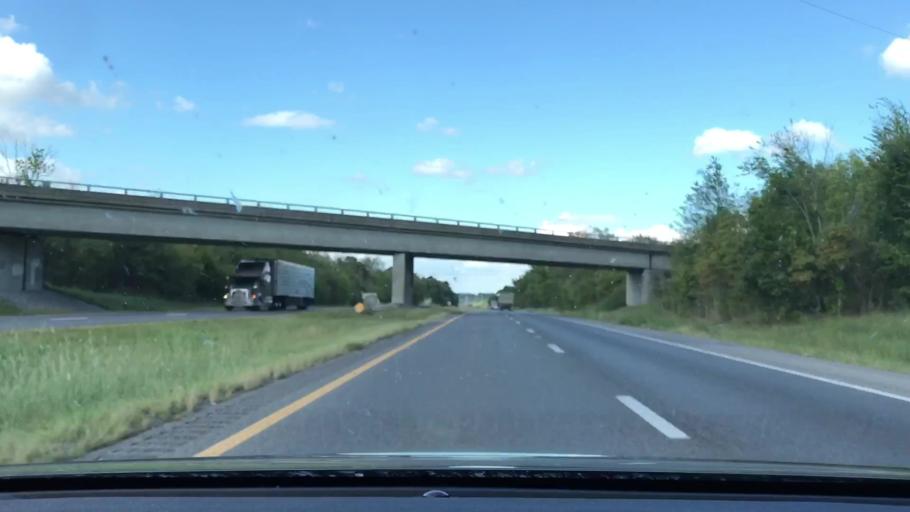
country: US
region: Kentucky
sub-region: Marshall County
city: Calvert City
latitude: 36.9674
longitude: -88.3473
